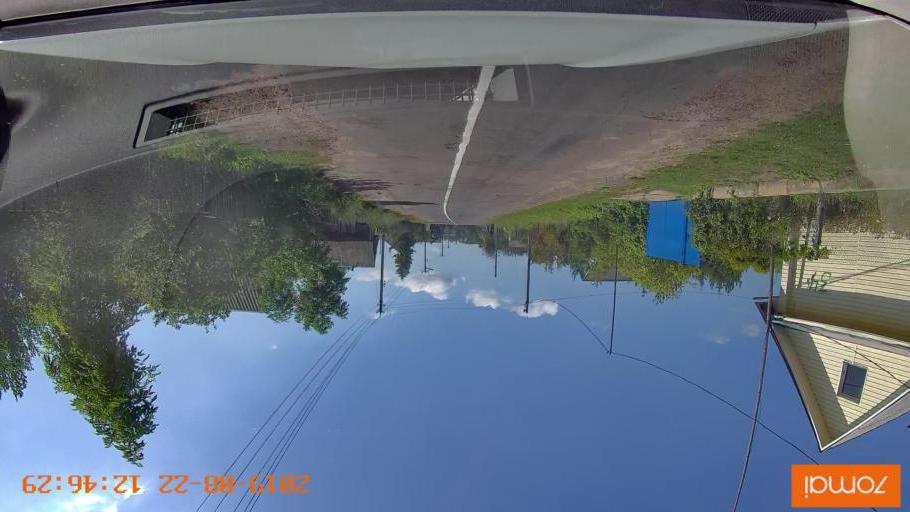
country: BY
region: Minsk
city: Prawdzinski
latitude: 53.4589
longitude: 27.6296
